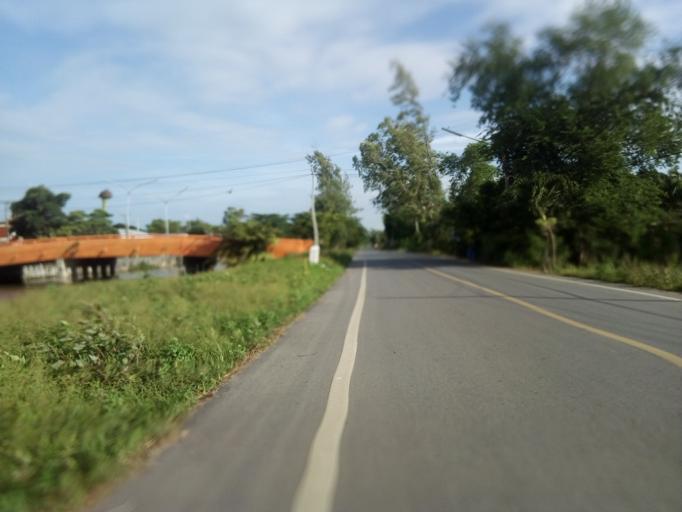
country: TH
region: Pathum Thani
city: Nong Suea
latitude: 14.1151
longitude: 100.8460
